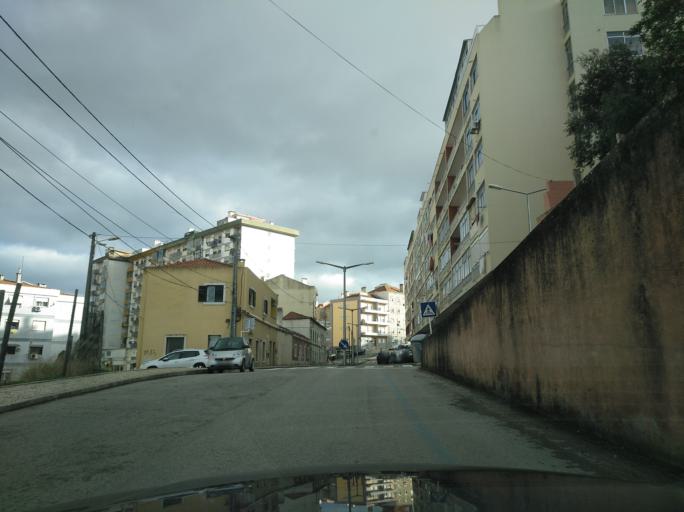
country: PT
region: Lisbon
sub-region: Loures
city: Sacavem
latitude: 38.7938
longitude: -9.1110
